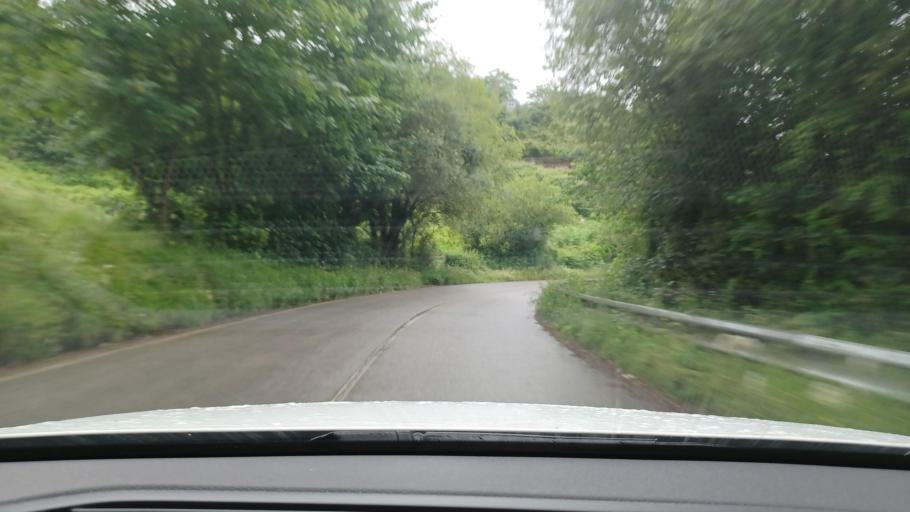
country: ES
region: Asturias
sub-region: Province of Asturias
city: Castandiello
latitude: 43.3142
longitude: -5.9263
